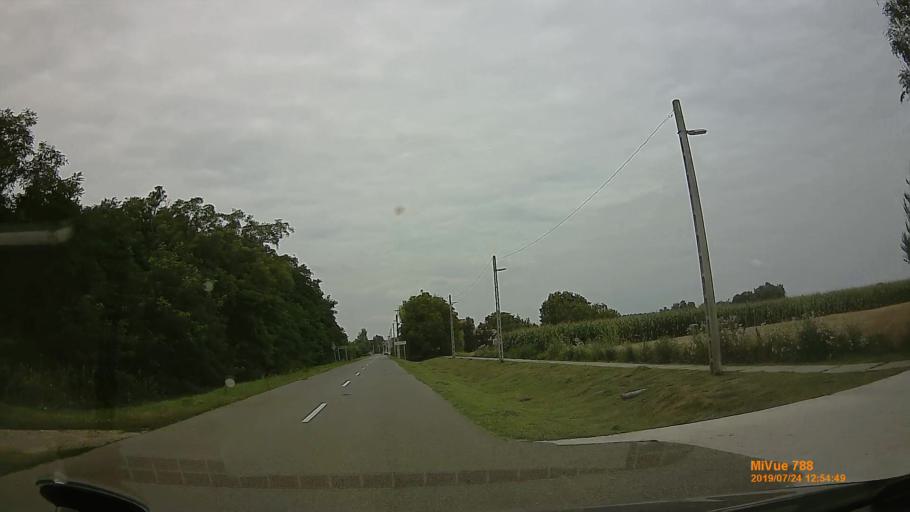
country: HU
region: Szabolcs-Szatmar-Bereg
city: Aranyosapati
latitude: 48.2196
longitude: 22.2956
